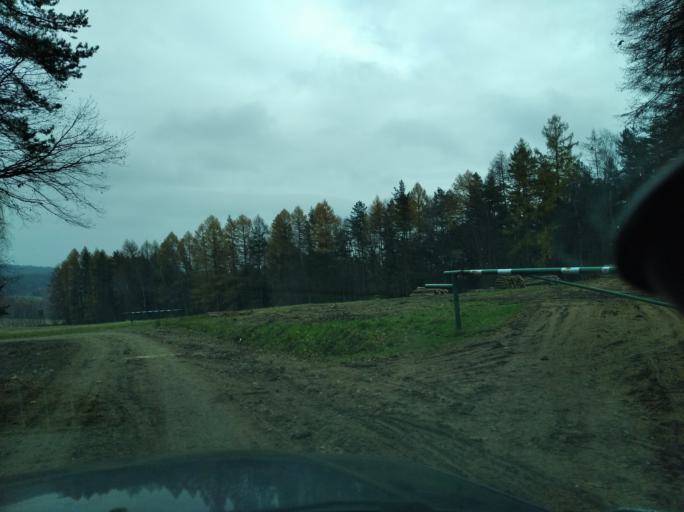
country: PL
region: Subcarpathian Voivodeship
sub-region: Powiat strzyzowski
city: Wysoka Strzyzowska
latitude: 49.7952
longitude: 21.7791
